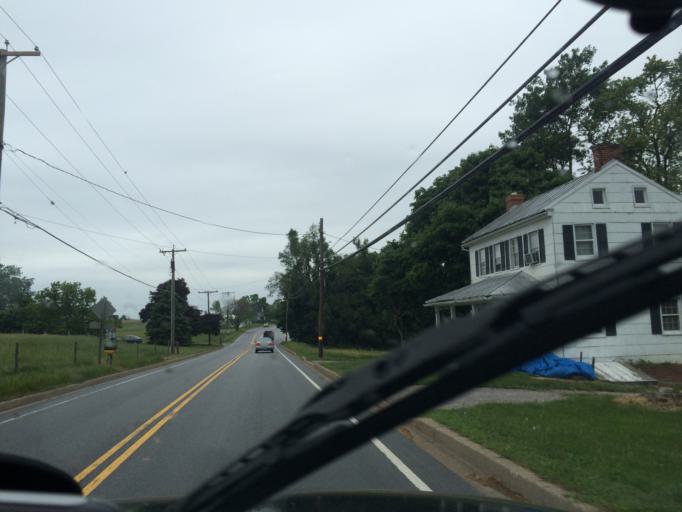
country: US
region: Maryland
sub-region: Carroll County
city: Westminster
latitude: 39.5246
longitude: -76.9908
